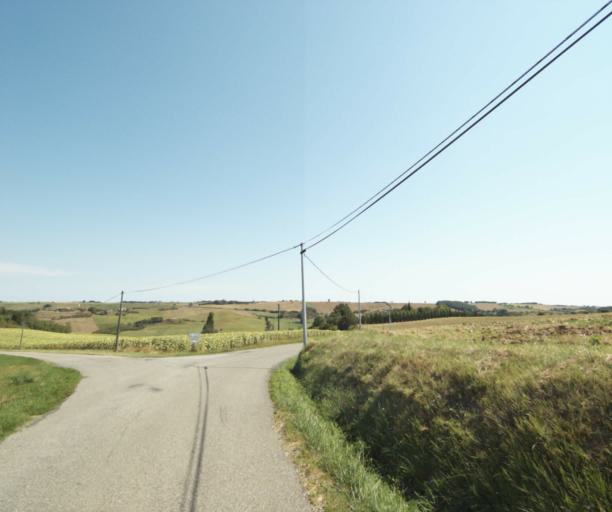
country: FR
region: Midi-Pyrenees
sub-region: Departement de l'Ariege
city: Lezat-sur-Leze
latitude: 43.2413
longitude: 1.3935
